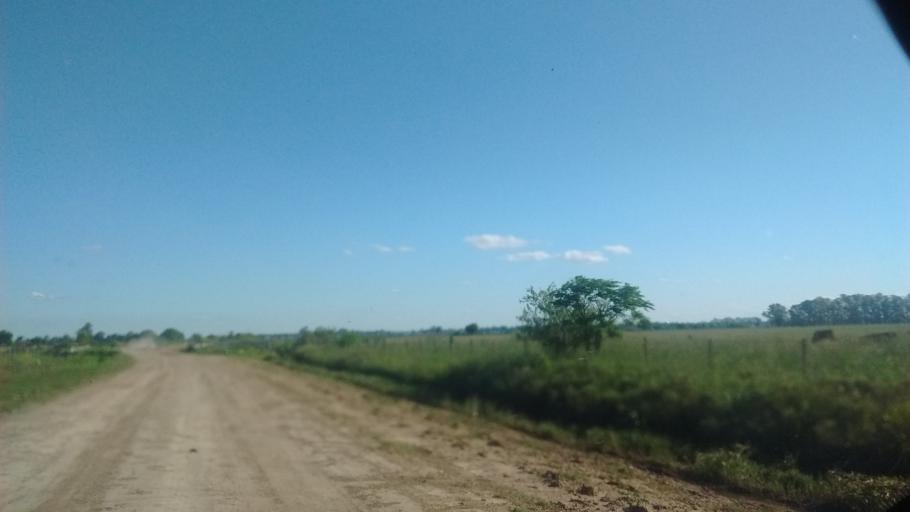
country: AR
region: Santa Fe
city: Funes
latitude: -32.8853
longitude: -60.7981
